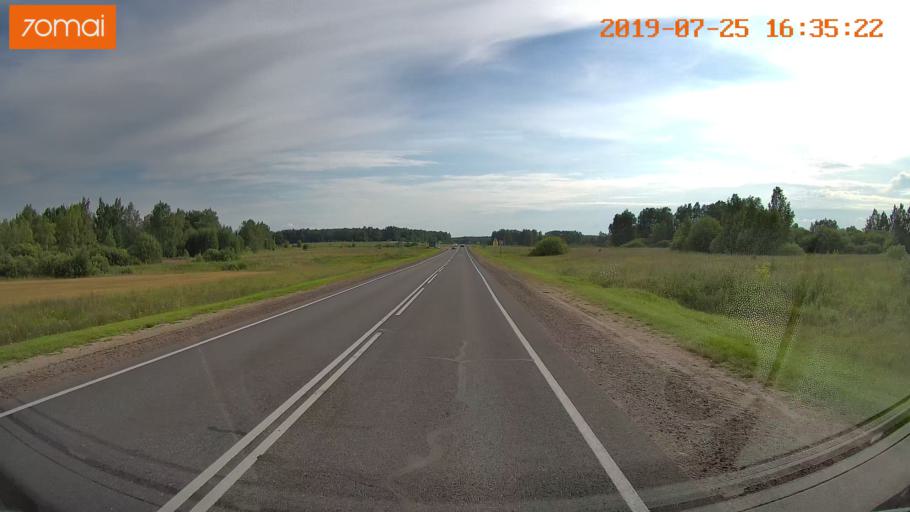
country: RU
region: Ivanovo
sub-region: Privolzhskiy Rayon
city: Ples
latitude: 57.4062
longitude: 41.4217
